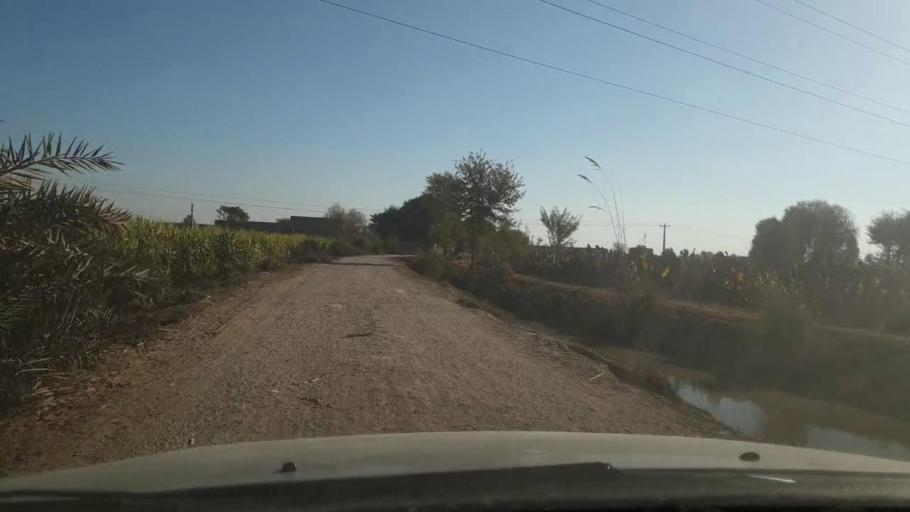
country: PK
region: Sindh
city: Adilpur
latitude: 27.9536
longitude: 69.2194
